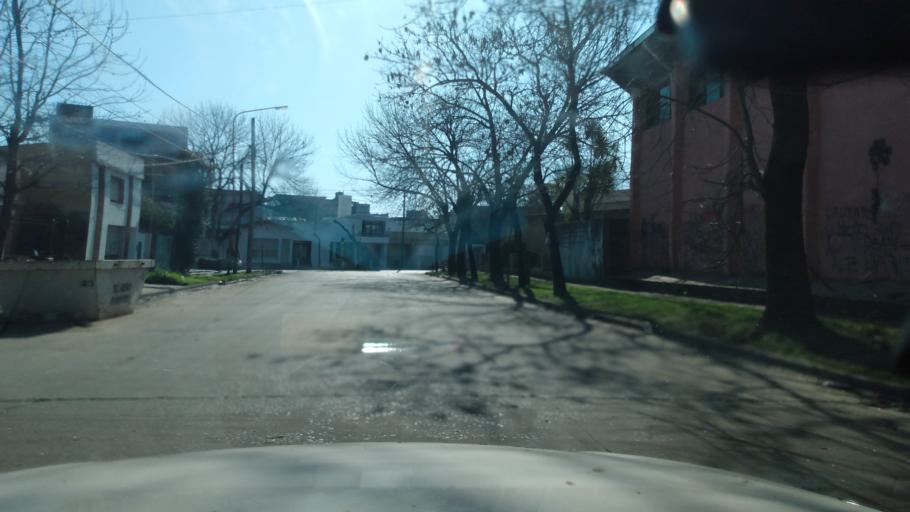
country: AR
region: Buenos Aires
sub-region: Partido de Lujan
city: Lujan
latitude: -34.5720
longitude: -59.1143
